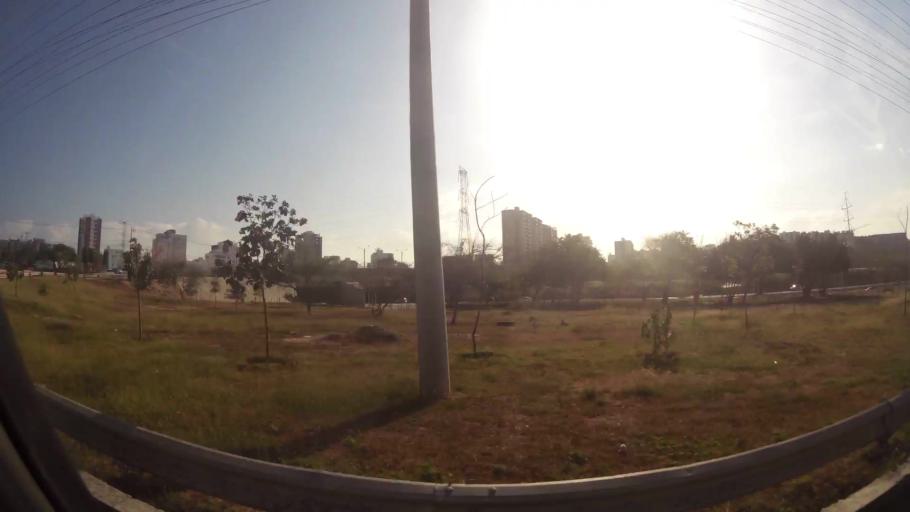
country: CO
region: Atlantico
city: Barranquilla
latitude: 11.0113
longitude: -74.8415
